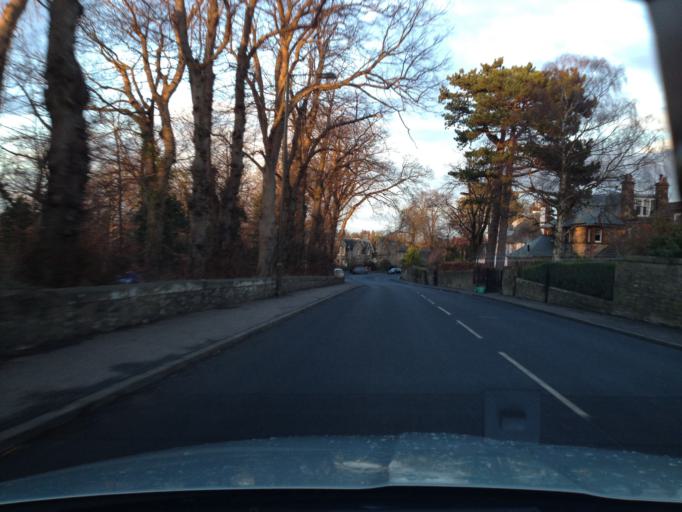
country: GB
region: Scotland
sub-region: Edinburgh
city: Colinton
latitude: 55.9055
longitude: -3.2598
